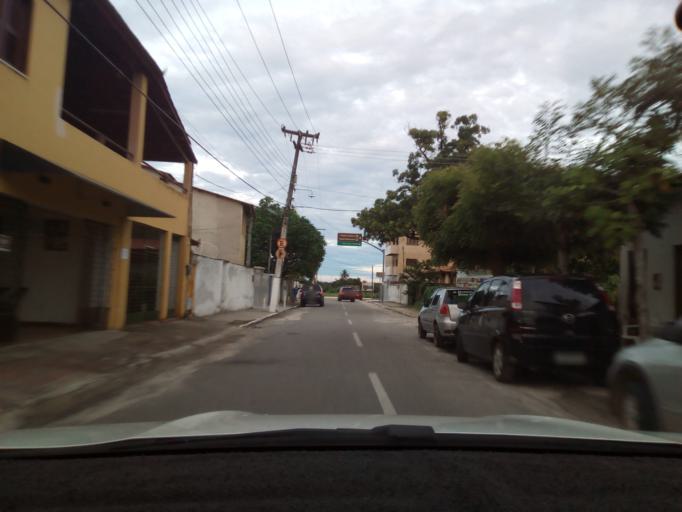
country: BR
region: Ceara
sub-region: Beberibe
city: Beberibe
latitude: -4.1833
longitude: -38.1263
